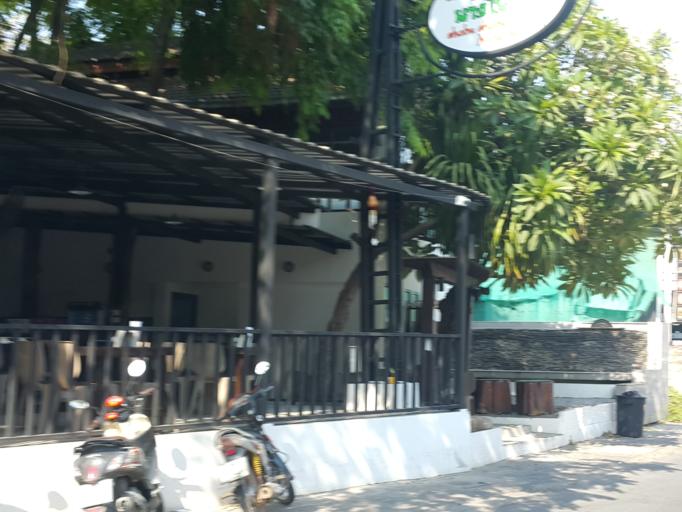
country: TH
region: Phitsanulok
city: Phitsanulok
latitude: 16.8107
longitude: 100.2629
